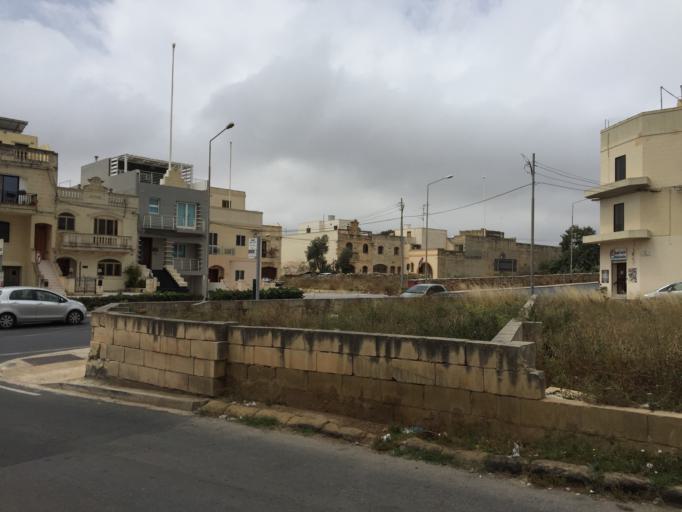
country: MT
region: Haz-Zabbar
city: Zabbar
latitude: 35.8713
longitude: 14.5349
